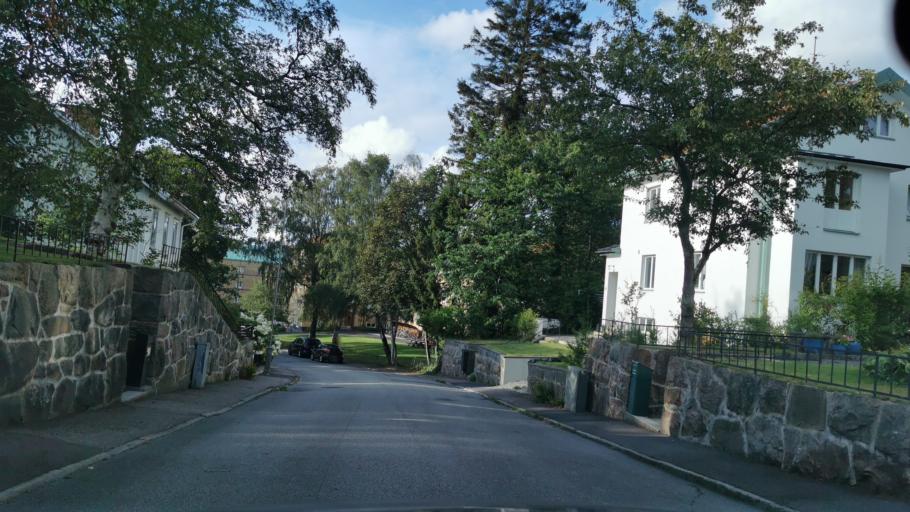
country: SE
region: Vaestra Goetaland
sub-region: Goteborg
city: Majorna
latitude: 57.6785
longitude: 11.9303
